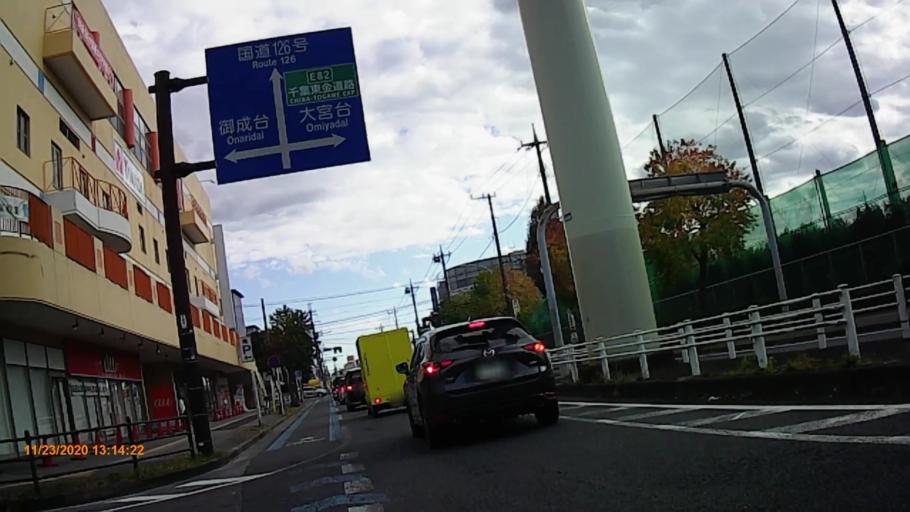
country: JP
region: Chiba
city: Yotsukaido
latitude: 35.6221
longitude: 140.1890
